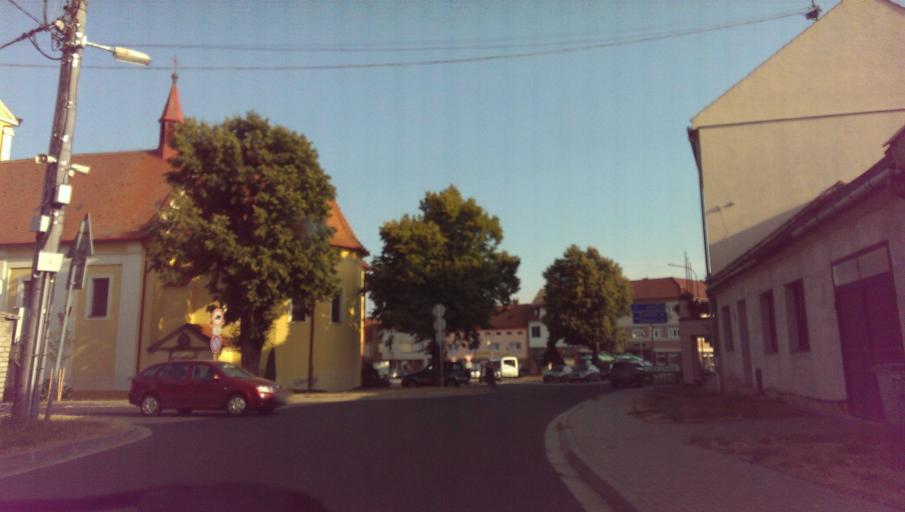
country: CZ
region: Zlin
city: Korycany
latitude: 49.1056
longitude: 17.1643
